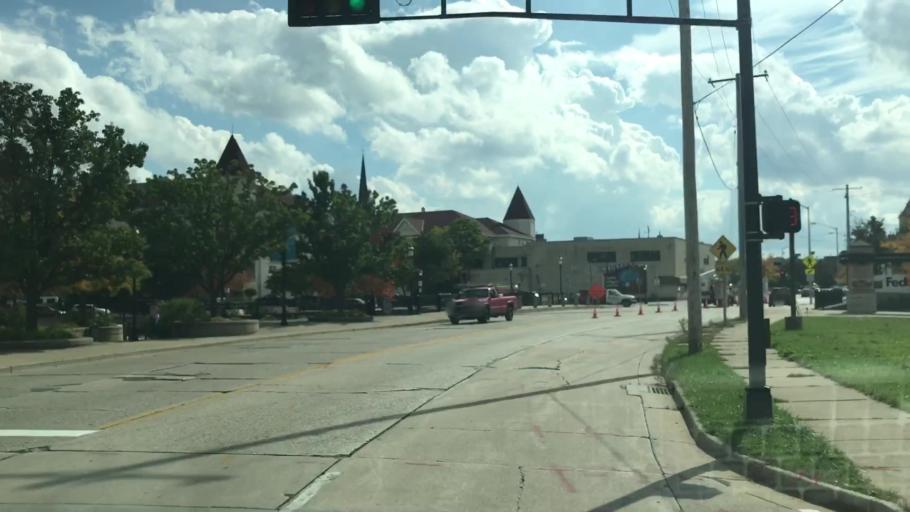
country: US
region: Wisconsin
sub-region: Waukesha County
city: Waukesha
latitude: 43.0137
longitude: -88.2300
